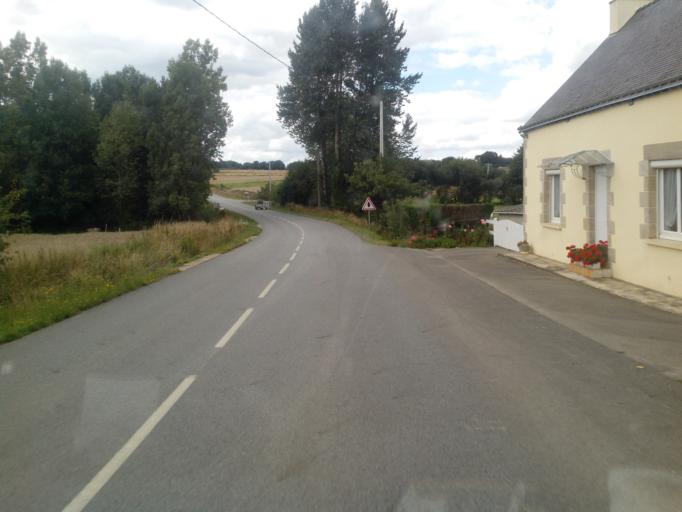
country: FR
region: Brittany
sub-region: Departement du Morbihan
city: Guilliers
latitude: 48.0692
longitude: -2.4241
